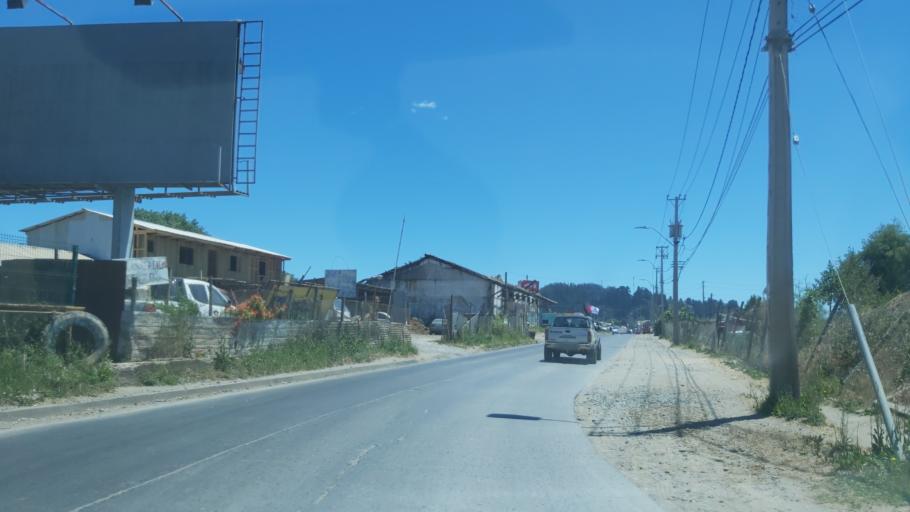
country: CL
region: Maule
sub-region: Provincia de Talca
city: Constitucion
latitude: -35.3375
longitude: -72.4028
